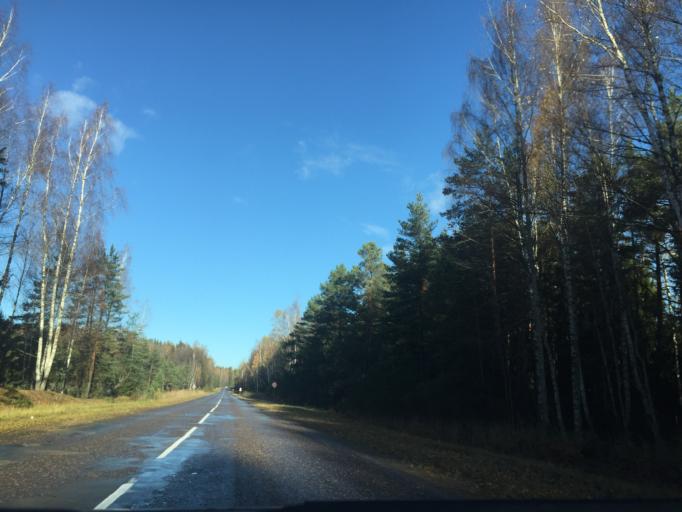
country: LV
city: Tireli
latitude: 56.8751
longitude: 23.5401
